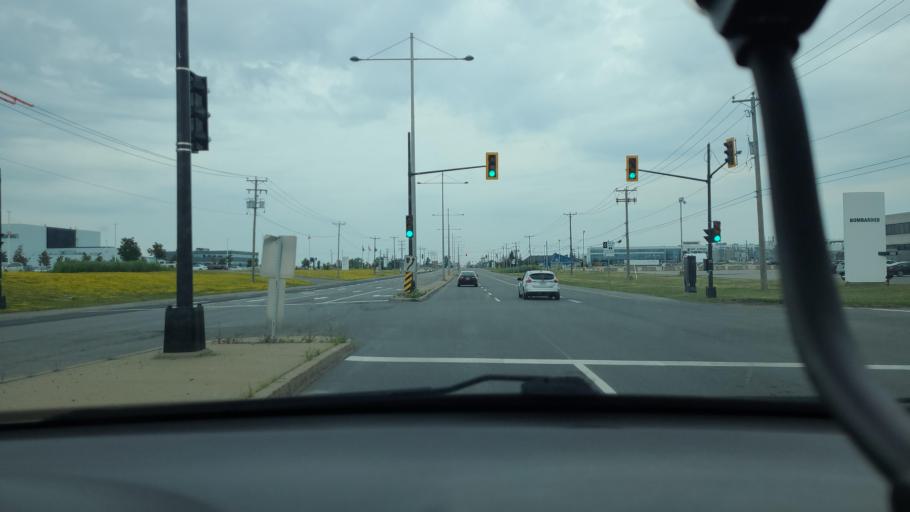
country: CA
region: Quebec
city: Dorval
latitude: 45.4762
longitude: -73.7305
